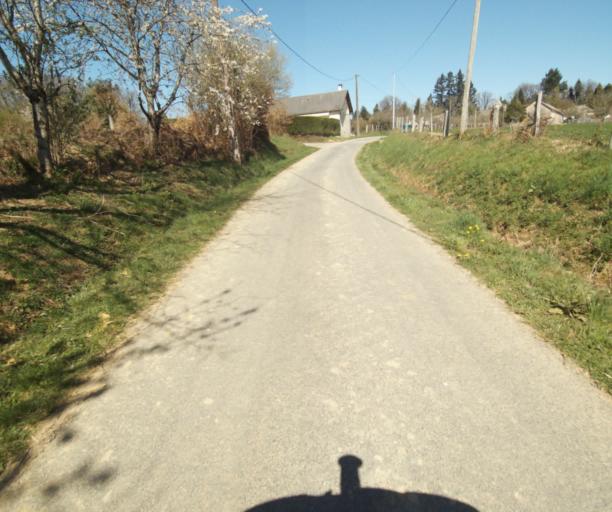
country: FR
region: Limousin
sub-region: Departement de la Correze
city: Saint-Mexant
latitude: 45.3150
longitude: 1.6565
